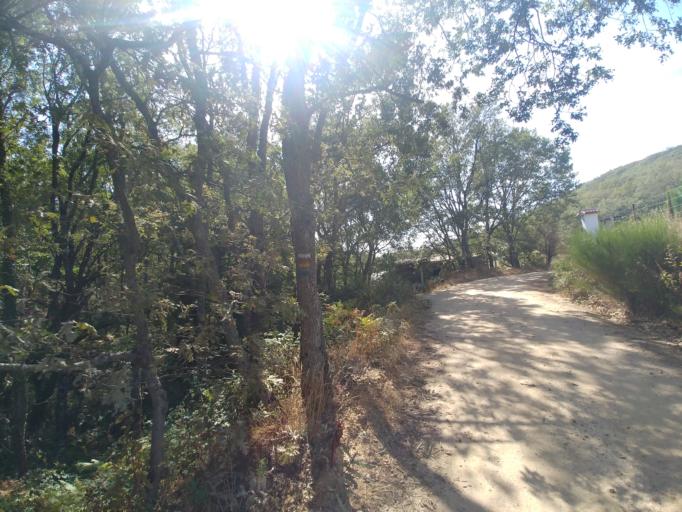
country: ES
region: Extremadura
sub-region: Provincia de Caceres
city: Garganta la Olla
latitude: 40.0999
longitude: -5.7425
